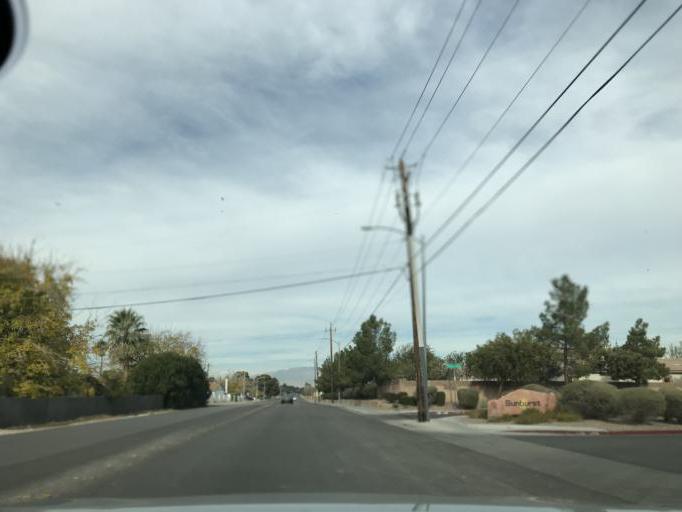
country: US
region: Nevada
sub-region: Clark County
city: Las Vegas
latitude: 36.2085
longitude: -115.2155
